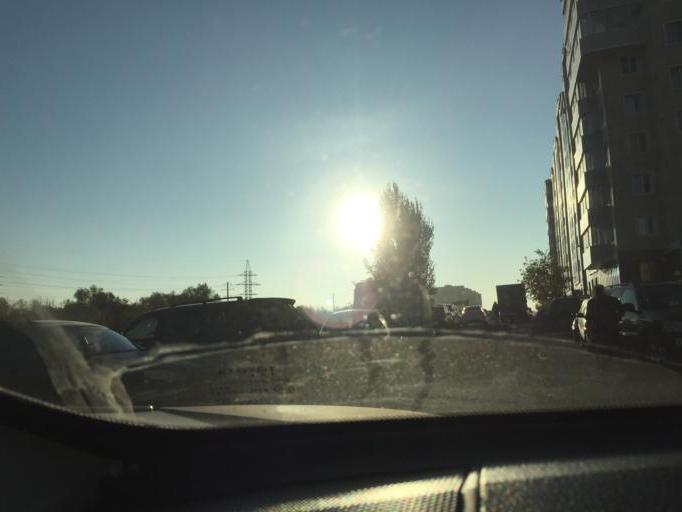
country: KZ
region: Astana Qalasy
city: Astana
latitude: 51.1578
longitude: 71.5105
